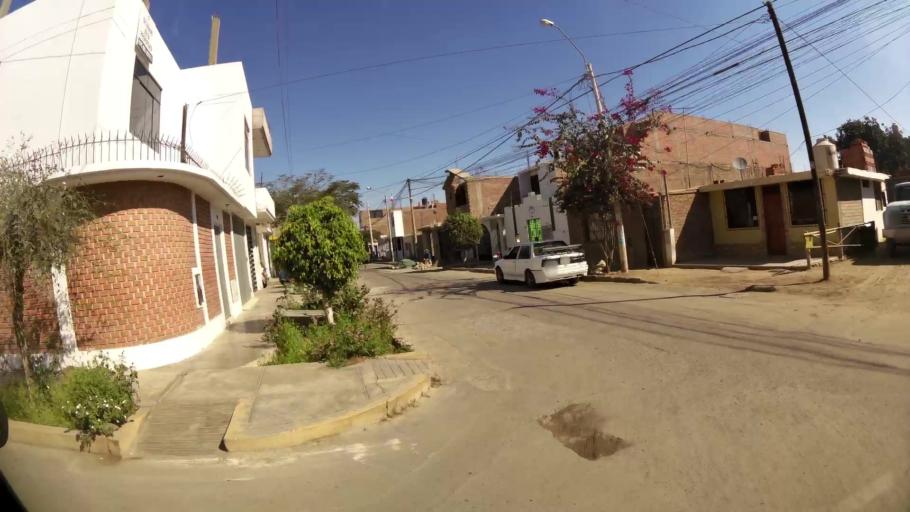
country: PE
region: Ica
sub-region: Provincia de Ica
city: La Tinguina
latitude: -14.0378
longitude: -75.7124
